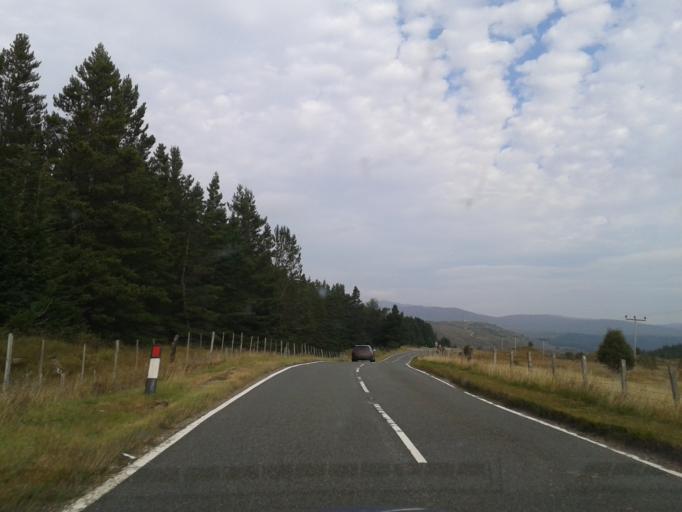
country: GB
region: Scotland
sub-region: Highland
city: Spean Bridge
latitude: 57.1357
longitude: -4.9551
